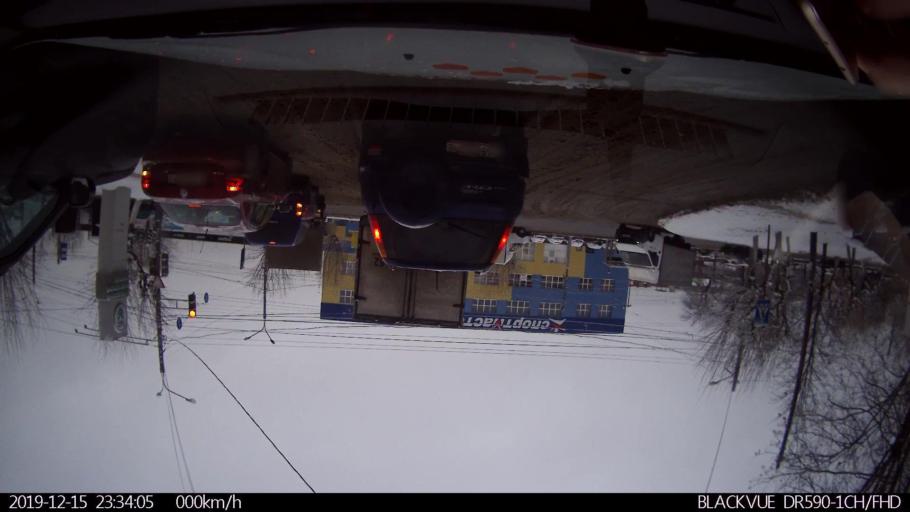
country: RU
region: Nizjnij Novgorod
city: Nizhniy Novgorod
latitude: 56.3160
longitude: 43.9119
